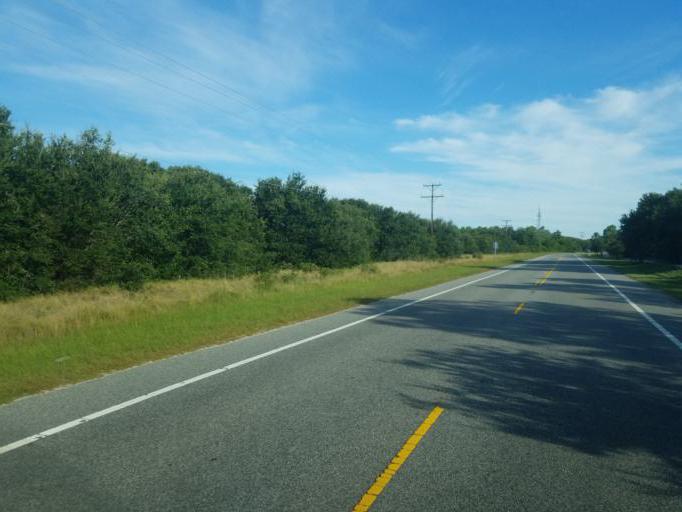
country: US
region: North Carolina
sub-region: Dare County
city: Southern Shores
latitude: 36.3147
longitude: -75.8126
